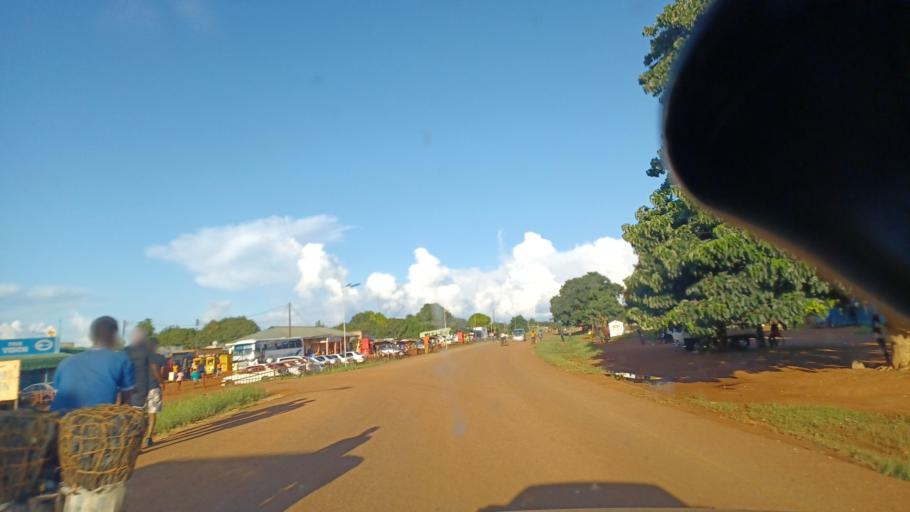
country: ZM
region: North-Western
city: Kalengwa
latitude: -13.1370
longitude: 25.0063
